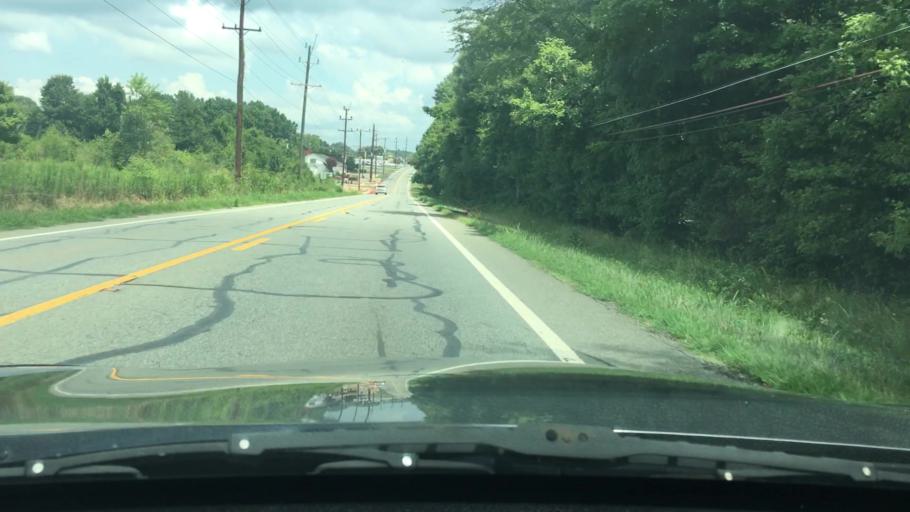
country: US
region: North Carolina
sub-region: Alamance County
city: Mebane
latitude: 36.0982
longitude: -79.2803
